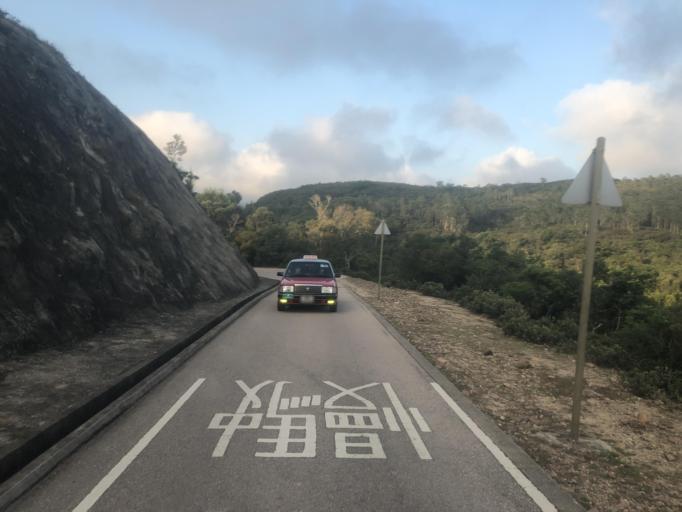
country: HK
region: Sai Kung
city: Sai Kung
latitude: 22.3619
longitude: 114.3538
